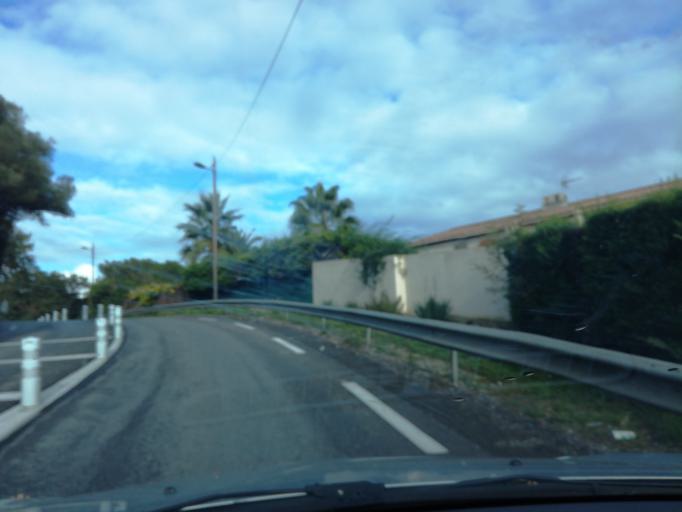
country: FR
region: Provence-Alpes-Cote d'Azur
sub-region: Departement des Alpes-Maritimes
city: Pegomas
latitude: 43.6211
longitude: 6.9349
